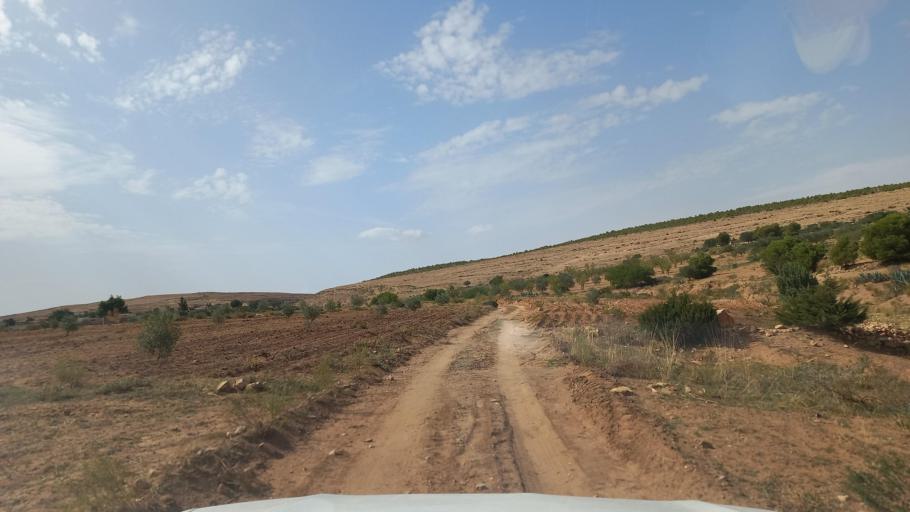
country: TN
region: Al Qasrayn
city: Kasserine
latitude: 35.3642
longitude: 8.8579
